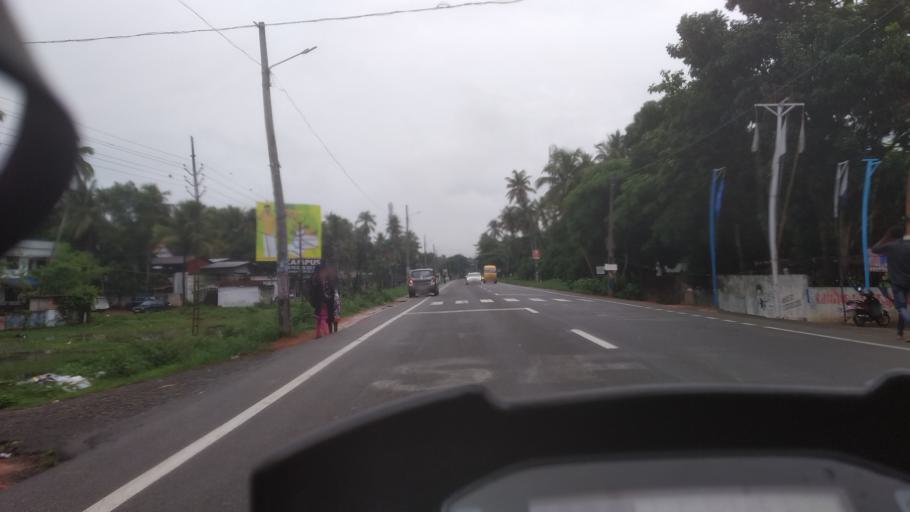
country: IN
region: Kerala
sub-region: Alappuzha
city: Kayankulam
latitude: 9.1790
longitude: 76.4930
